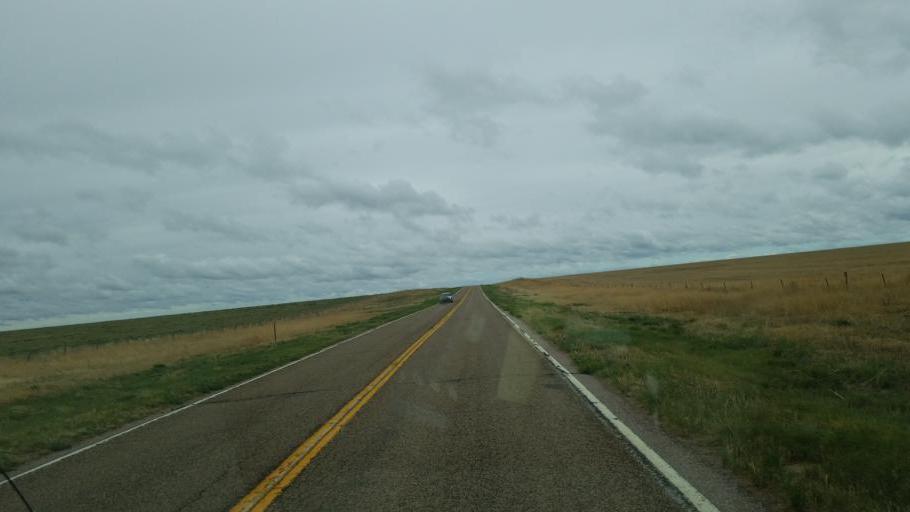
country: US
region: Colorado
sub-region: Lincoln County
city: Hugo
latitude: 38.8504
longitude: -103.4538
